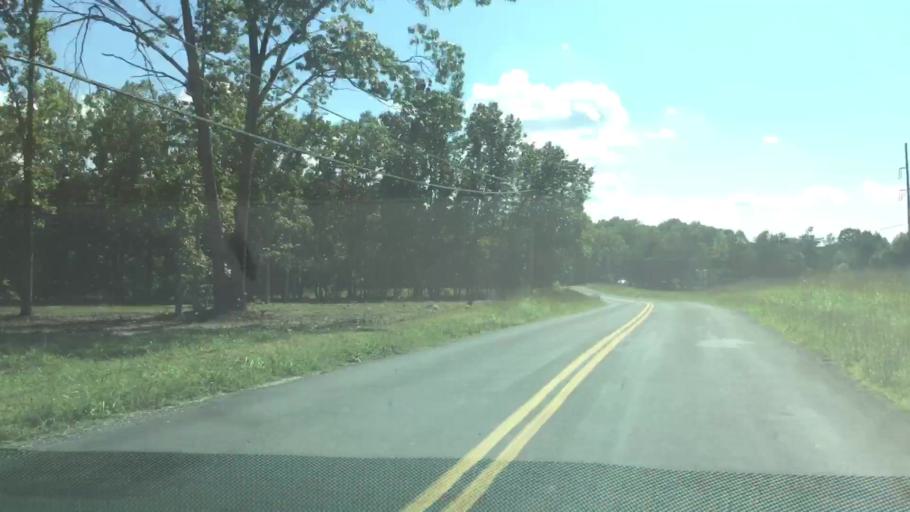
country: US
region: Virginia
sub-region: Appomattox County
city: Appomattox
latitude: 37.3149
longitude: -78.8435
